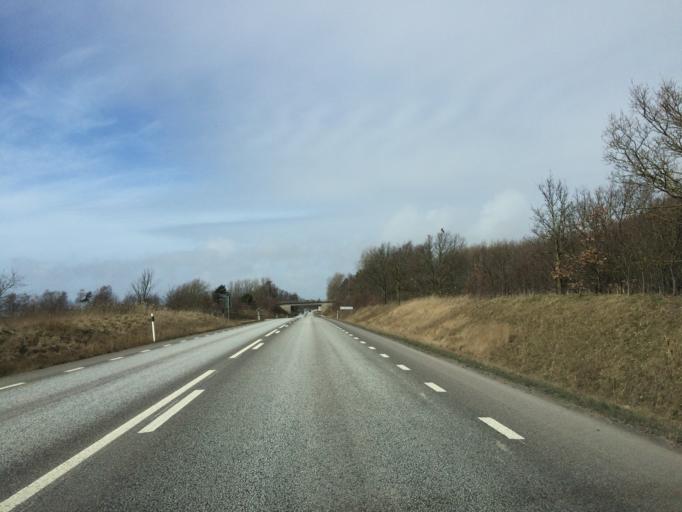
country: SE
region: Halland
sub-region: Halmstads Kommun
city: Troenninge
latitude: 56.6350
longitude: 12.9300
